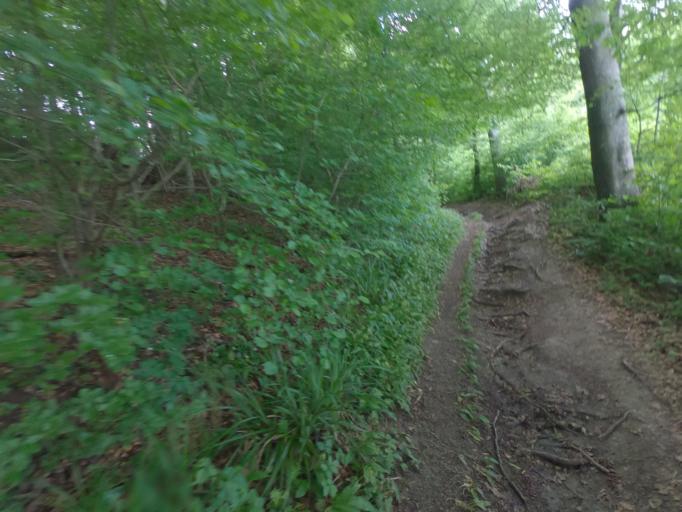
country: CH
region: Solothurn
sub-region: Bezirk Lebern
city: Langendorf
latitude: 47.2392
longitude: 7.5381
